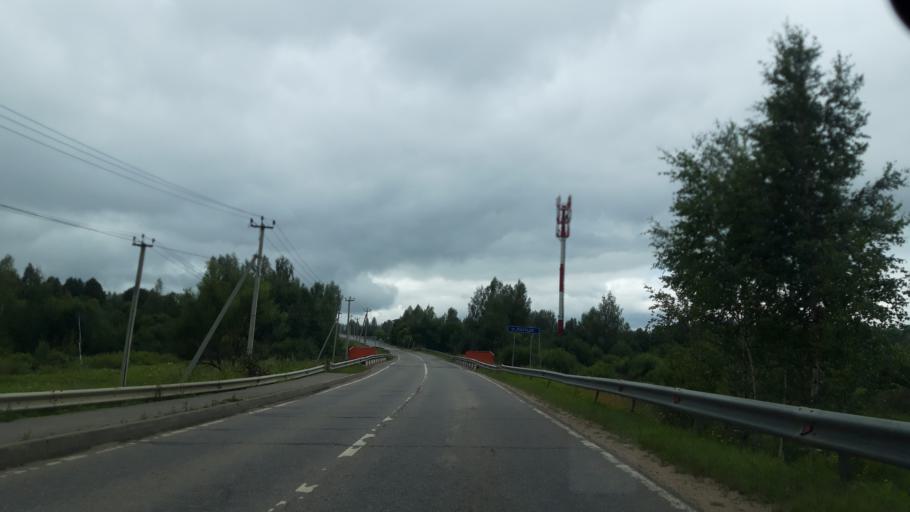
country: RU
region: Moskovskaya
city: Povarovo
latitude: 56.1036
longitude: 37.0133
